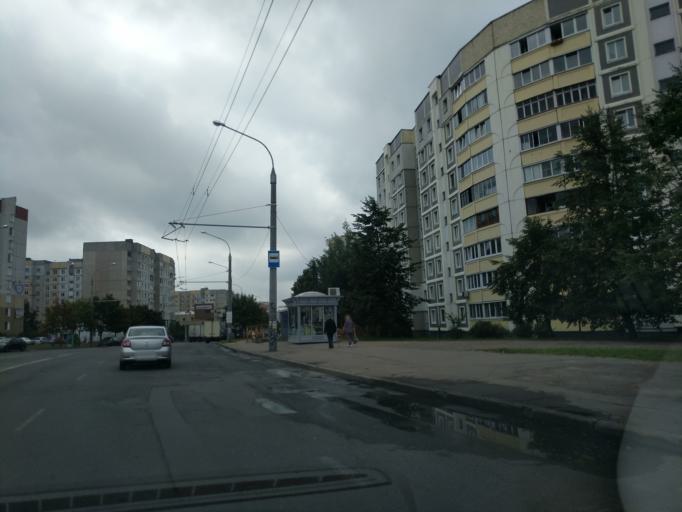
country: BY
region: Minsk
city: Novoye Medvezhino
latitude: 53.8858
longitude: 27.4373
